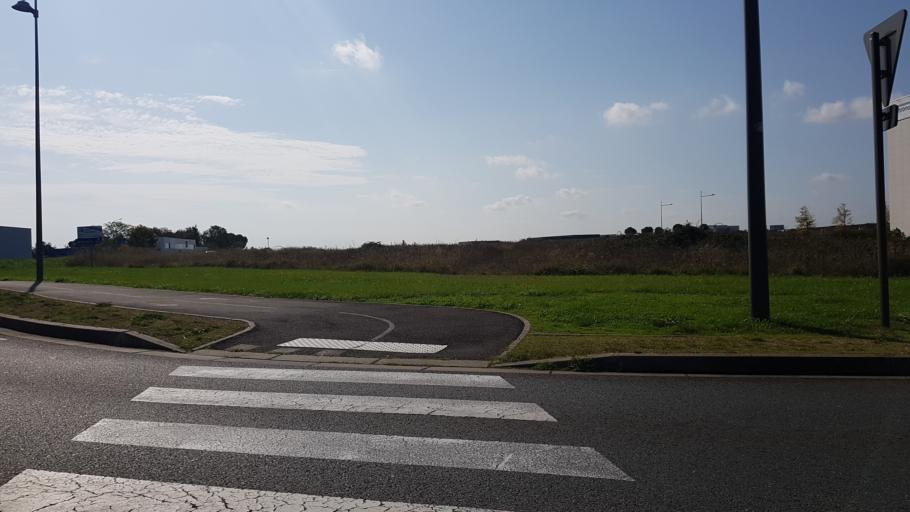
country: FR
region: Poitou-Charentes
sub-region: Departement de la Vienne
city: Chasseneuil-du-Poitou
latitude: 46.6552
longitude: 0.3619
